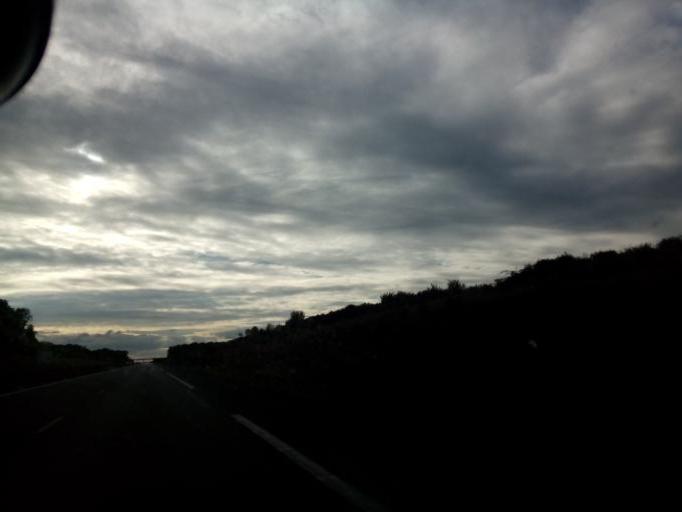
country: FR
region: Centre
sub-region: Departement d'Indre-et-Loire
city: Monts
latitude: 47.3070
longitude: 0.6267
